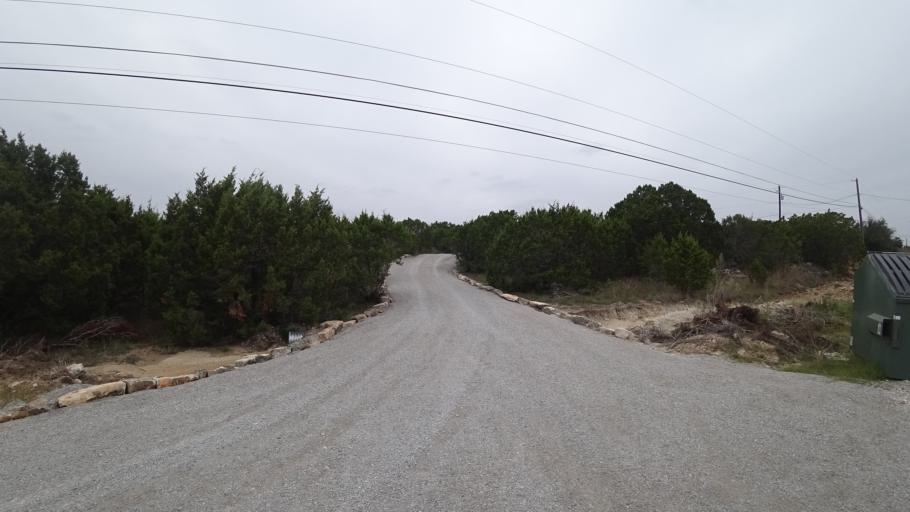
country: US
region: Texas
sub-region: Travis County
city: Lakeway
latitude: 30.3718
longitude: -97.9397
